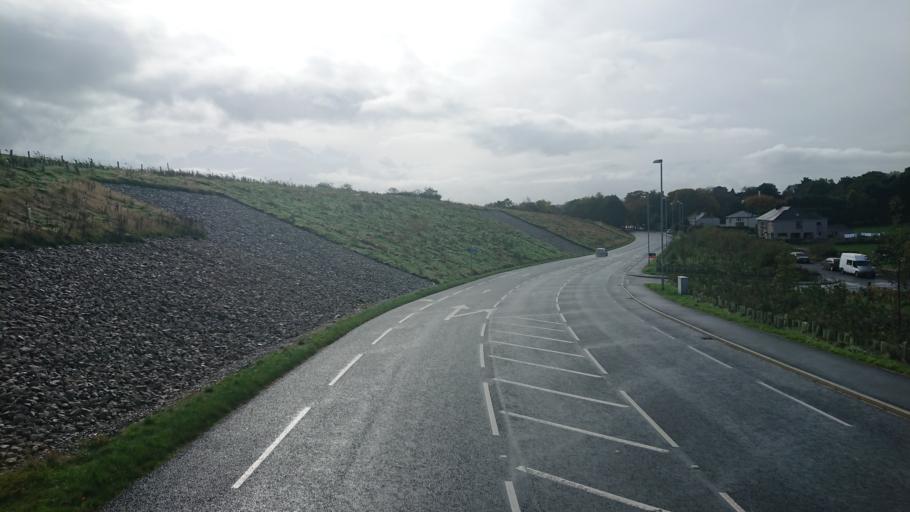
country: GB
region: England
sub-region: Lancashire
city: Bolton le Sands
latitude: 54.0713
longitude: -2.8006
